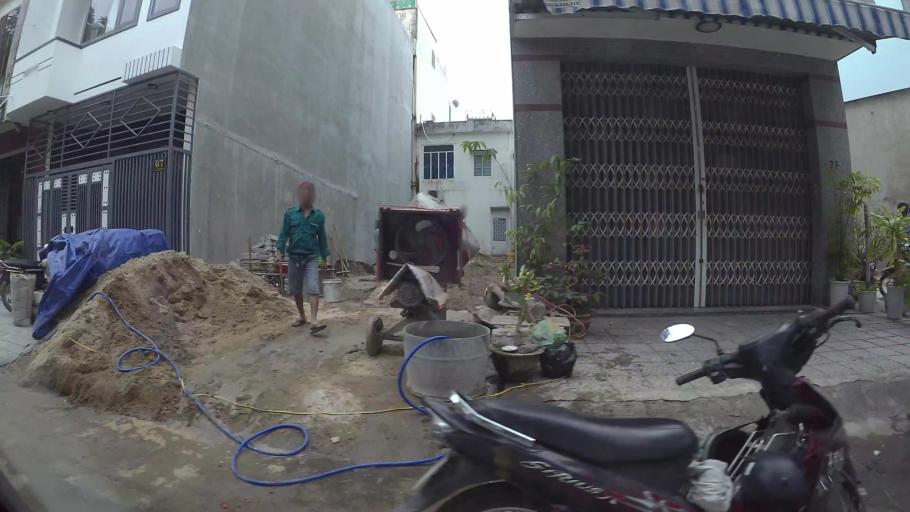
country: VN
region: Da Nang
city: Lien Chieu
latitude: 16.0786
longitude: 108.1657
